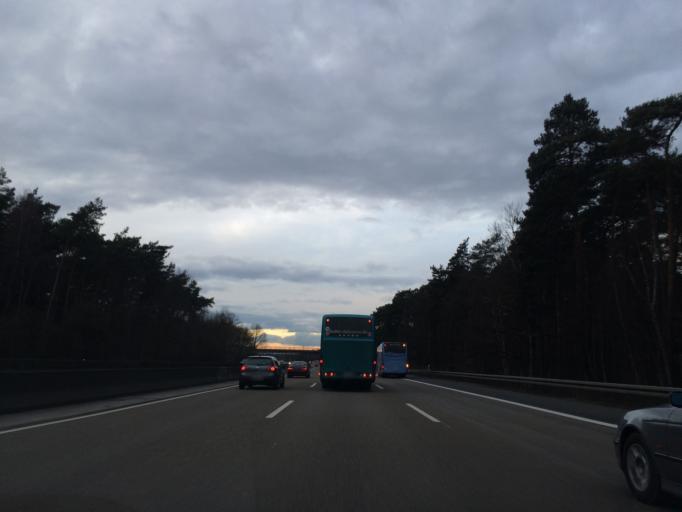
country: DE
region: Hesse
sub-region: Regierungsbezirk Darmstadt
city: Rodgau
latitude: 50.0532
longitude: 8.9162
